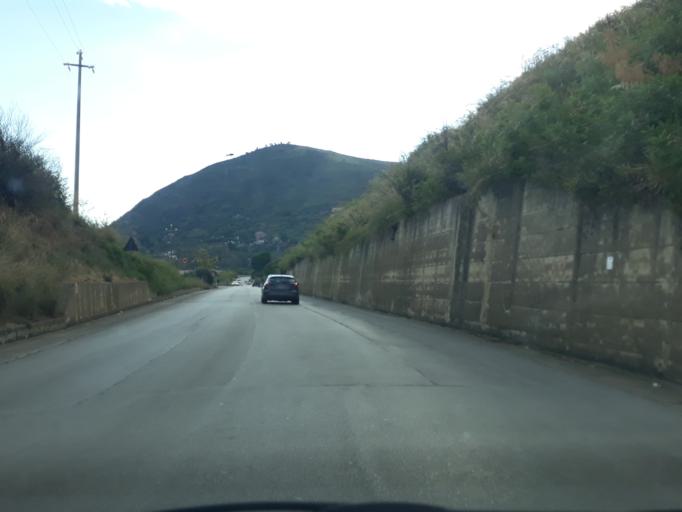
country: IT
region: Sicily
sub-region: Palermo
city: Cefalu
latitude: 38.0277
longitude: 14.0072
